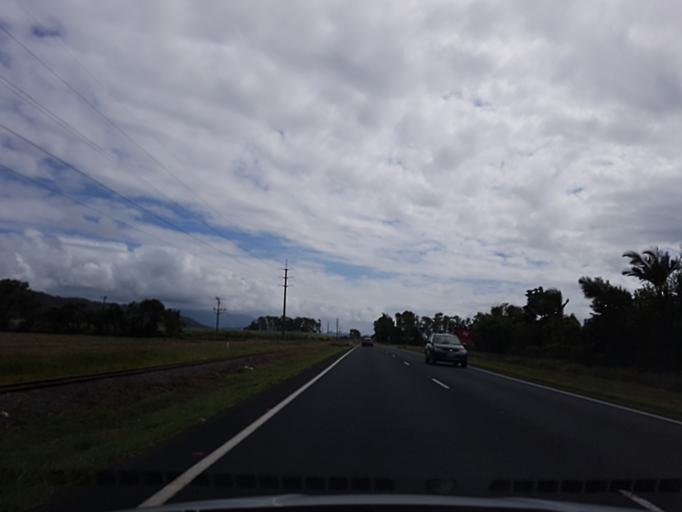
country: AU
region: Queensland
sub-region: Cairns
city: Port Douglas
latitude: -16.5113
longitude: 145.4435
